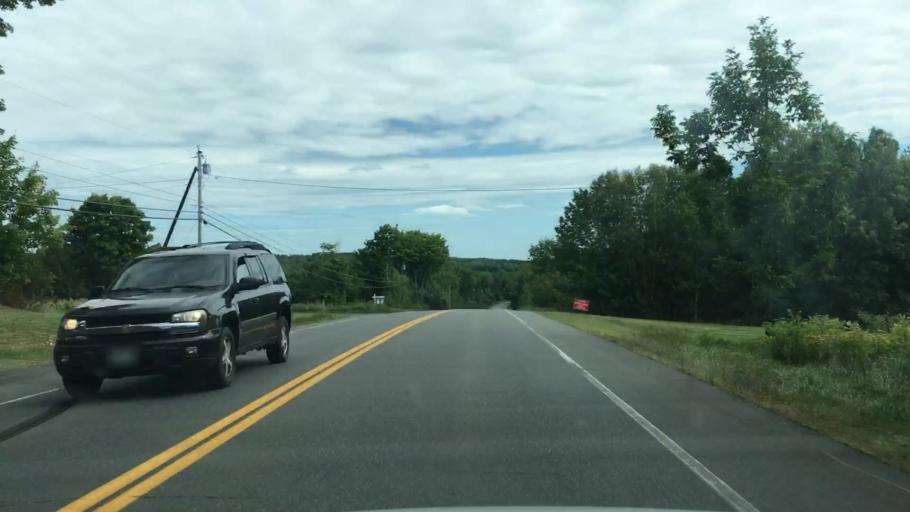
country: US
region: Maine
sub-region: Piscataquis County
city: Dover-Foxcroft
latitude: 45.2251
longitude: -69.1240
